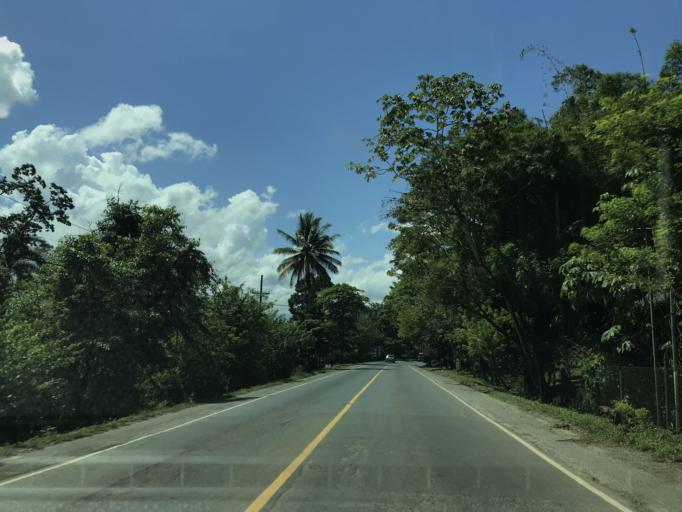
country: GT
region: Izabal
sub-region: Municipio de Puerto Barrios
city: Puerto Barrios
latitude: 15.6587
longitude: -88.5499
